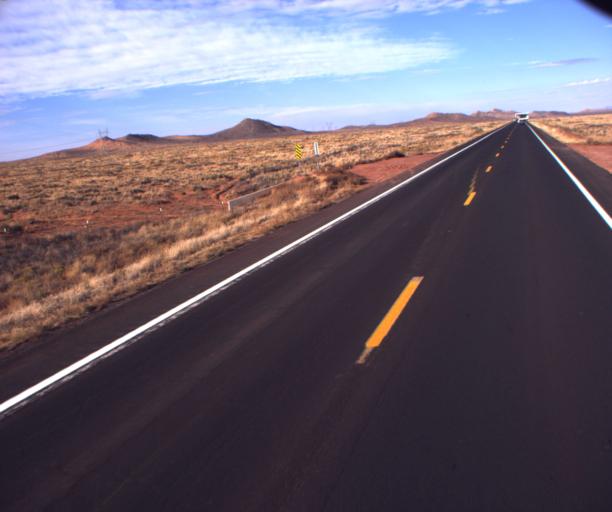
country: US
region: Arizona
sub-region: Apache County
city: Lukachukai
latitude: 36.9635
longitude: -109.4640
